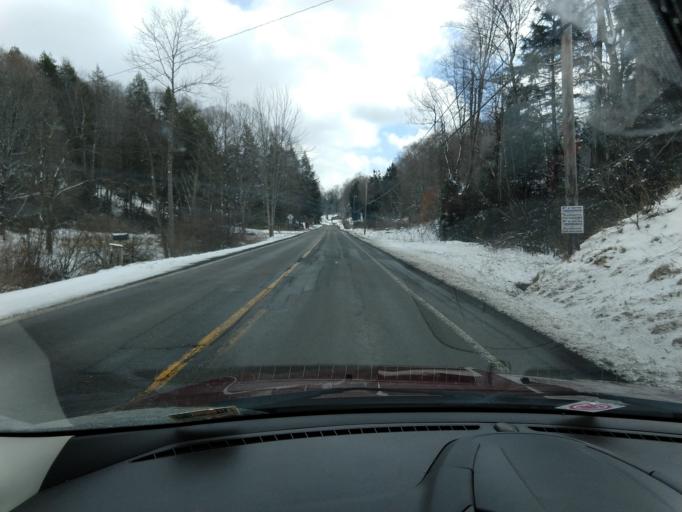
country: US
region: West Virginia
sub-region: Nicholas County
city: Craigsville
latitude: 38.3047
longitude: -80.6524
